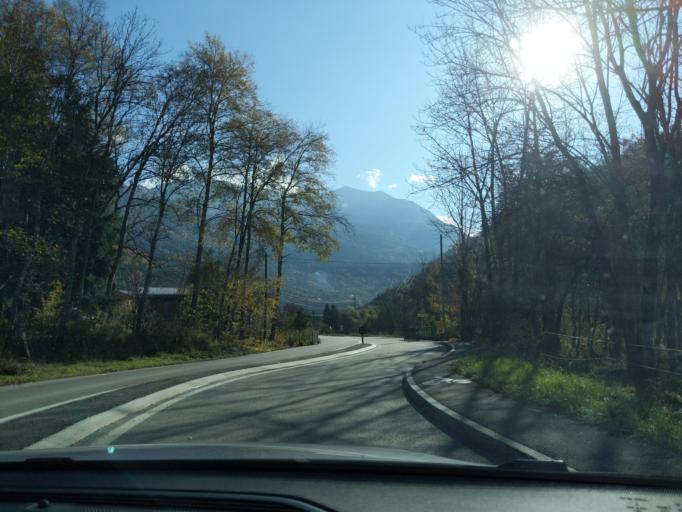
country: FR
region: Rhone-Alpes
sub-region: Departement de la Savoie
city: Seez
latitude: 45.6045
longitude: 6.8567
